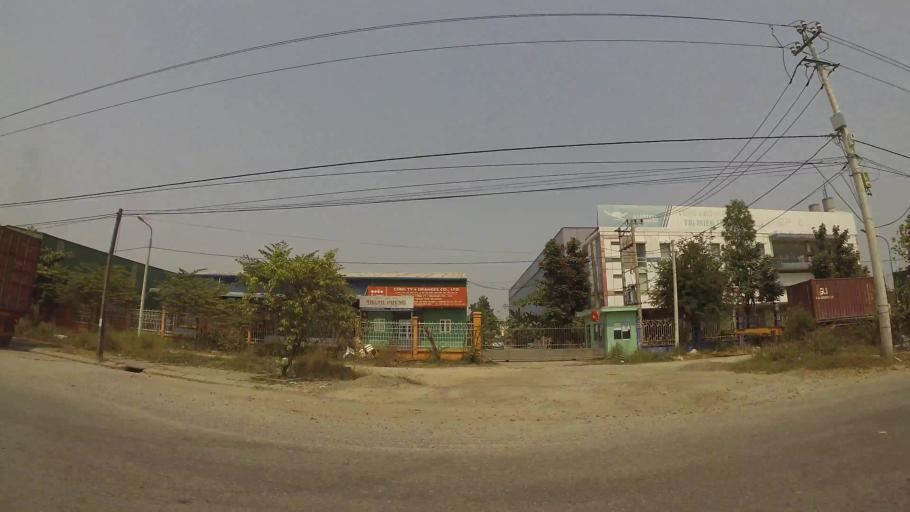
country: VN
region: Da Nang
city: Cam Le
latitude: 15.9895
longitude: 108.1978
